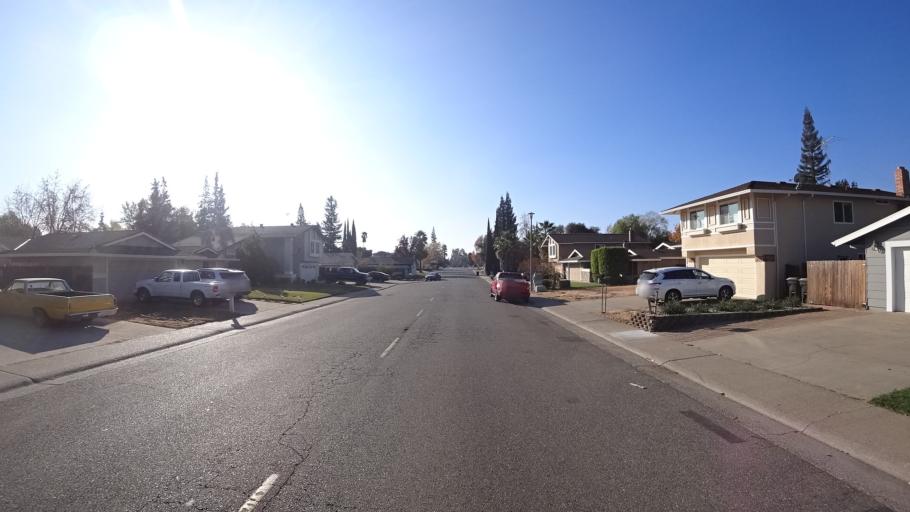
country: US
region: California
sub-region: Sacramento County
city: Citrus Heights
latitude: 38.7120
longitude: -121.2620
